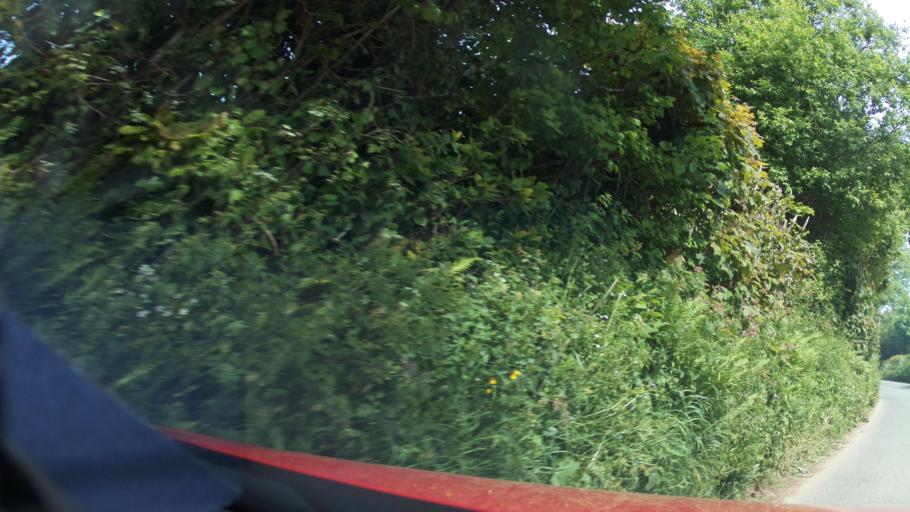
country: GB
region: England
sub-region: Devon
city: Kingsbridge
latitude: 50.3601
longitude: -3.7467
